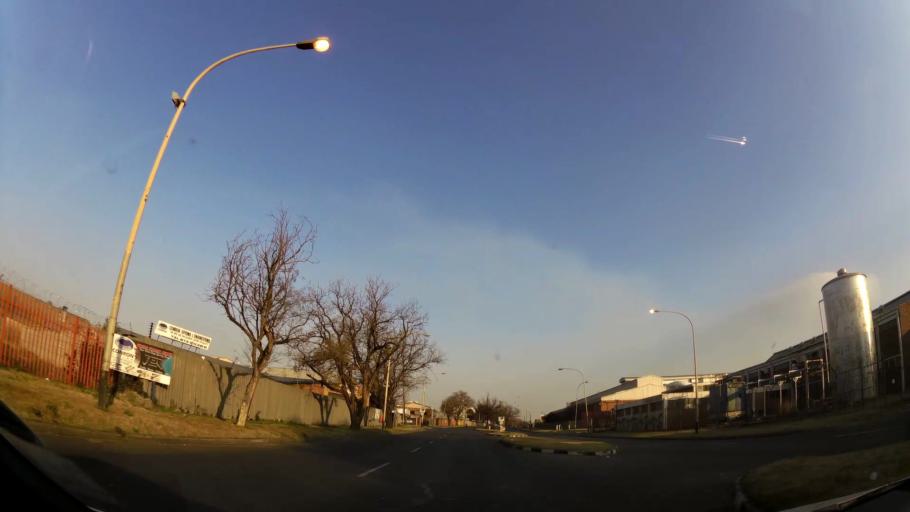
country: ZA
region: Gauteng
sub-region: Ekurhuleni Metropolitan Municipality
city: Springs
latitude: -26.2560
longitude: 28.4182
